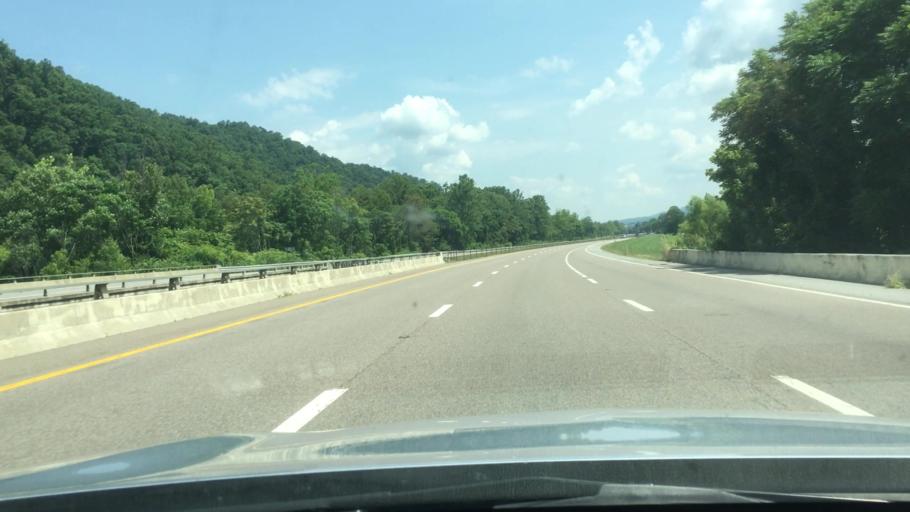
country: US
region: Tennessee
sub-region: Unicoi County
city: Banner Hill
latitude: 36.1267
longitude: -82.4437
